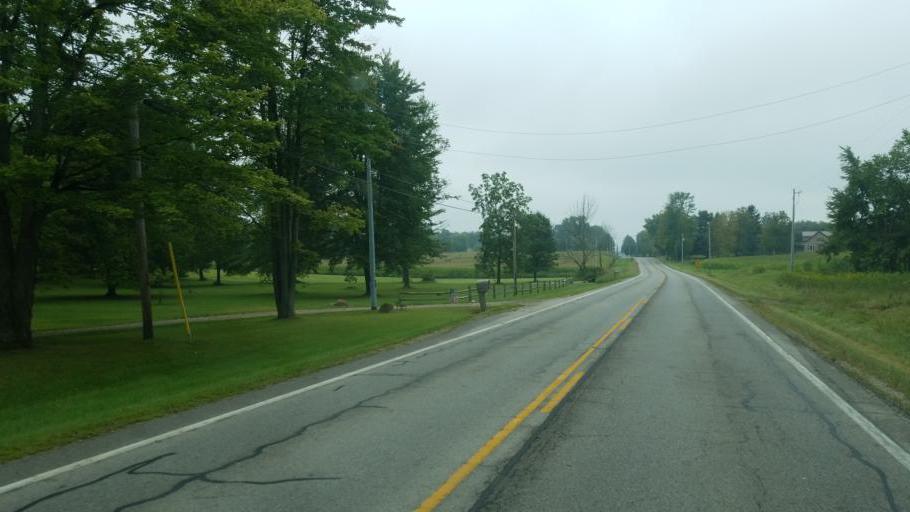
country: US
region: Ohio
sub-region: Knox County
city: Mount Vernon
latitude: 40.3193
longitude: -82.4599
